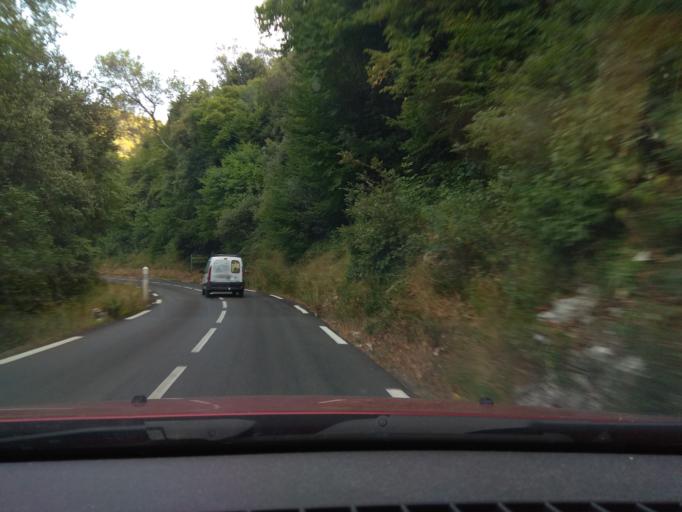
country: FR
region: Provence-Alpes-Cote d'Azur
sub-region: Departement des Alpes-Maritimes
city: La Colle-sur-Loup
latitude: 43.6857
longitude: 7.0713
